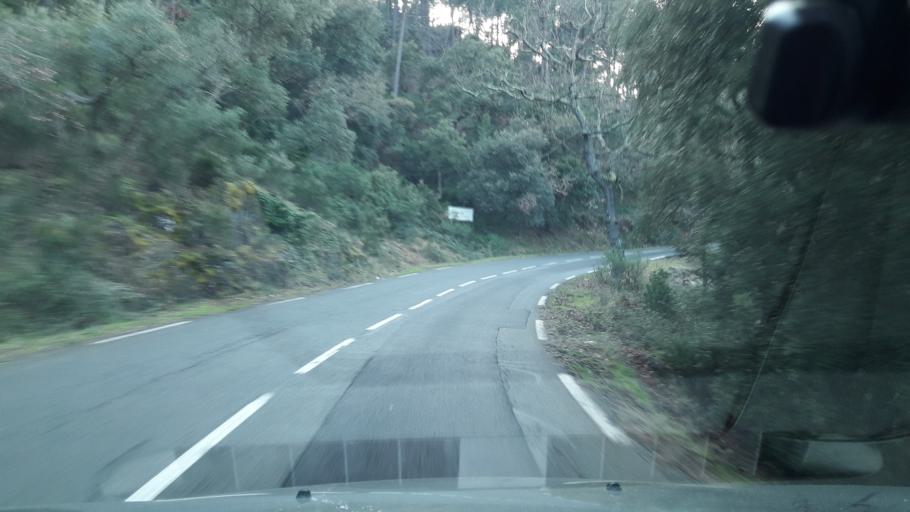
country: FR
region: Provence-Alpes-Cote d'Azur
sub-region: Departement du Var
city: Tanneron
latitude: 43.5180
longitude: 6.8510
